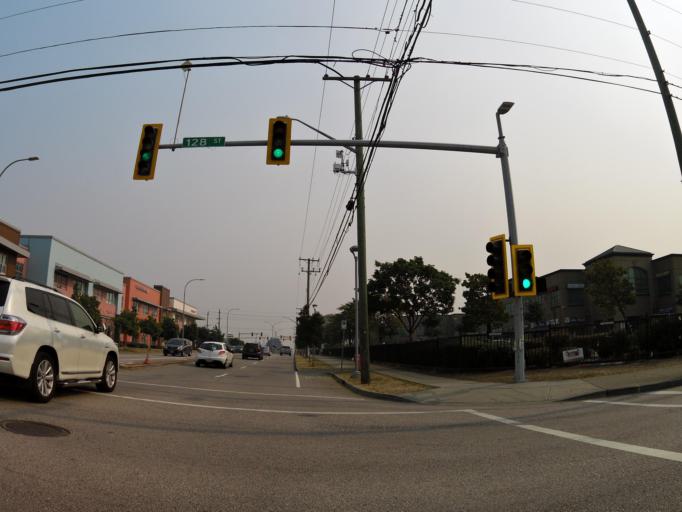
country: CA
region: British Columbia
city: Delta
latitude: 49.1481
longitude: -122.8680
